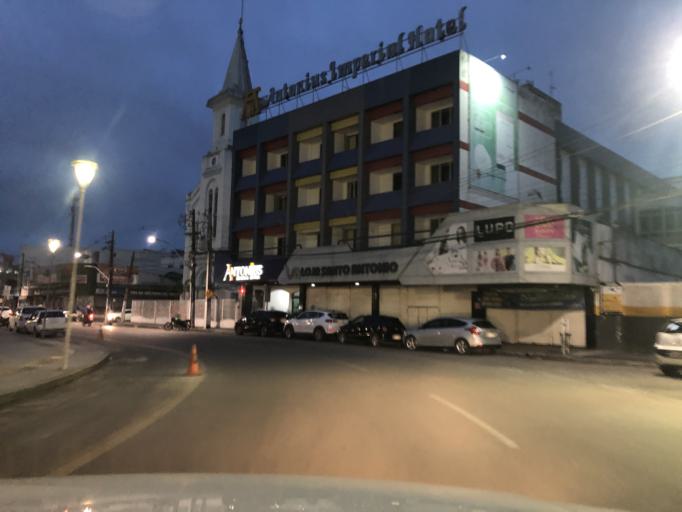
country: BR
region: Bahia
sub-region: Santo Antonio De Jesus
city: Santo Antonio de Jesus
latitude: -12.9691
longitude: -39.2633
